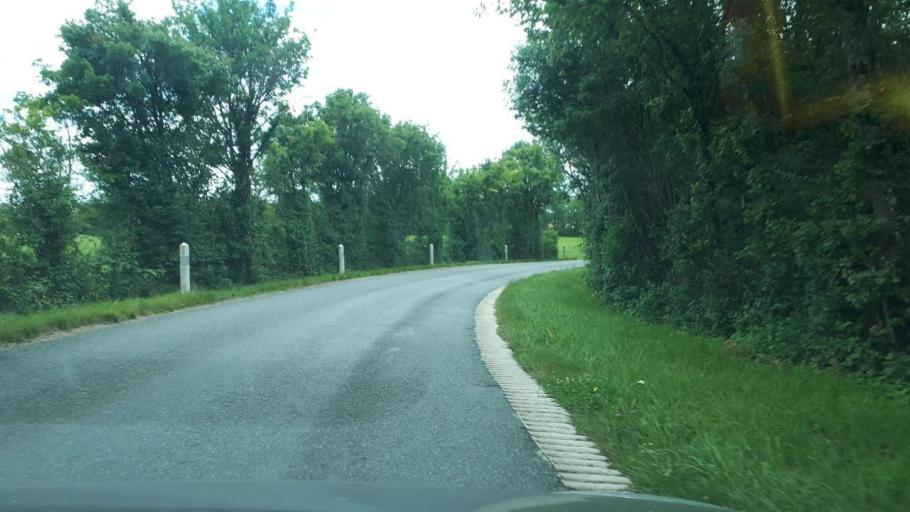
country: FR
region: Centre
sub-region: Departement du Cher
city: Rians
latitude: 47.2072
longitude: 2.6220
